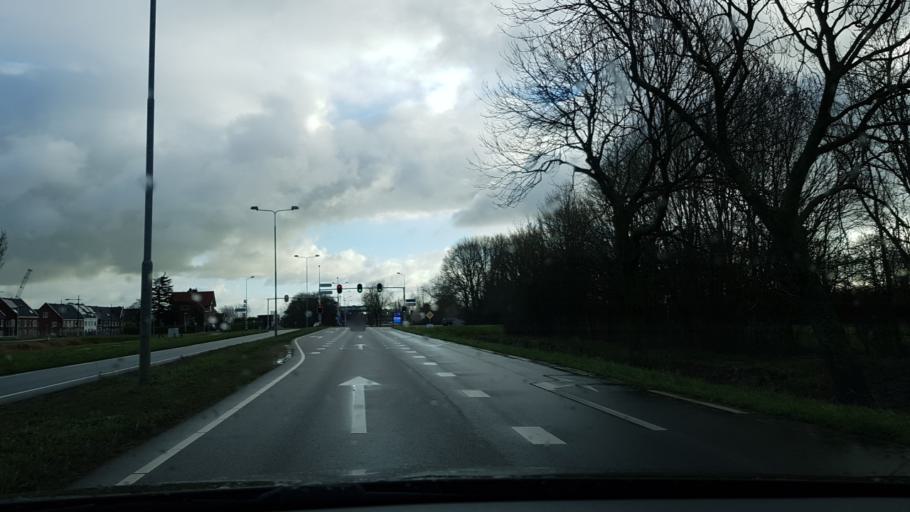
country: NL
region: North Holland
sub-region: Gemeente Uithoorn
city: Uithoorn
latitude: 52.2494
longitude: 4.7988
